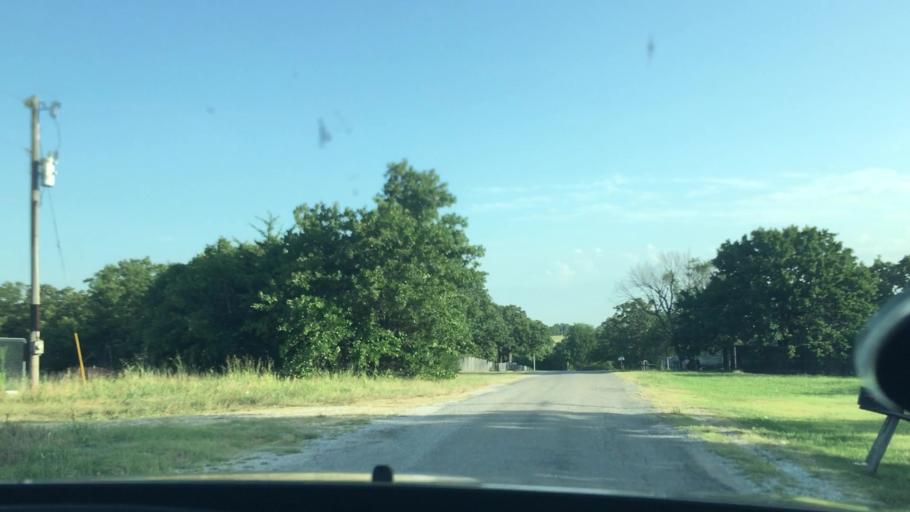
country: US
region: Oklahoma
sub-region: Pontotoc County
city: Byng
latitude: 34.8669
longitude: -96.6763
